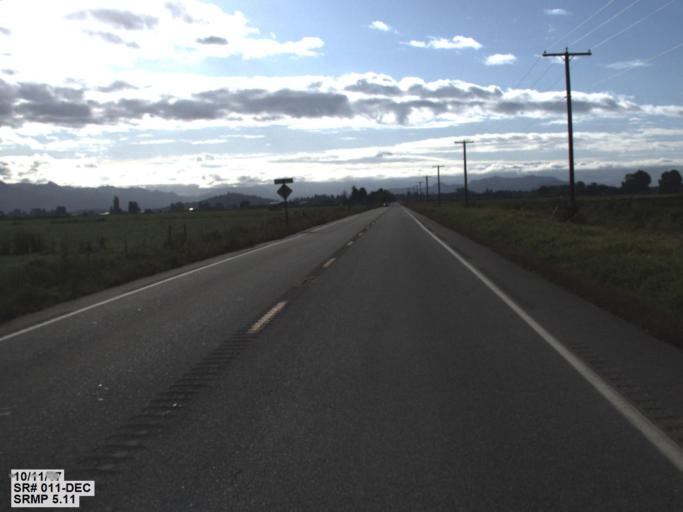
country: US
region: Washington
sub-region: Skagit County
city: Burlington
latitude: 48.5433
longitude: -122.4036
